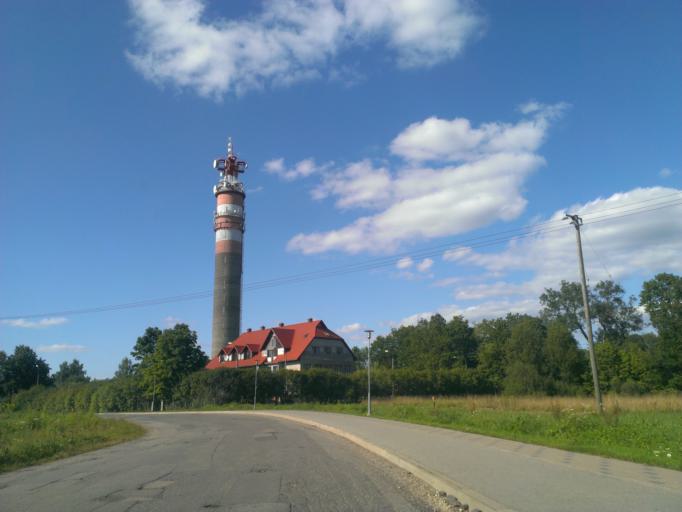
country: LV
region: Sigulda
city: Sigulda
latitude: 57.1619
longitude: 24.8819
